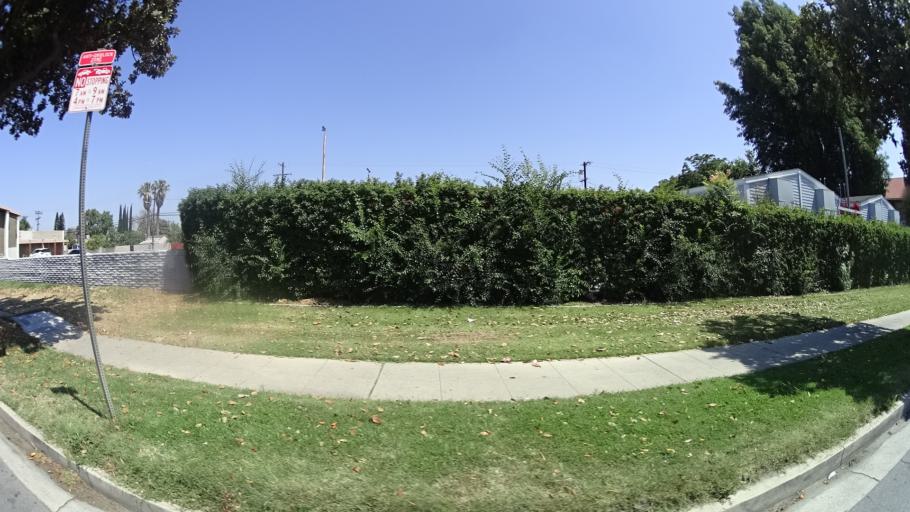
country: US
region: California
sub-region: Los Angeles County
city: Van Nuys
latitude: 34.2217
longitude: -118.4410
